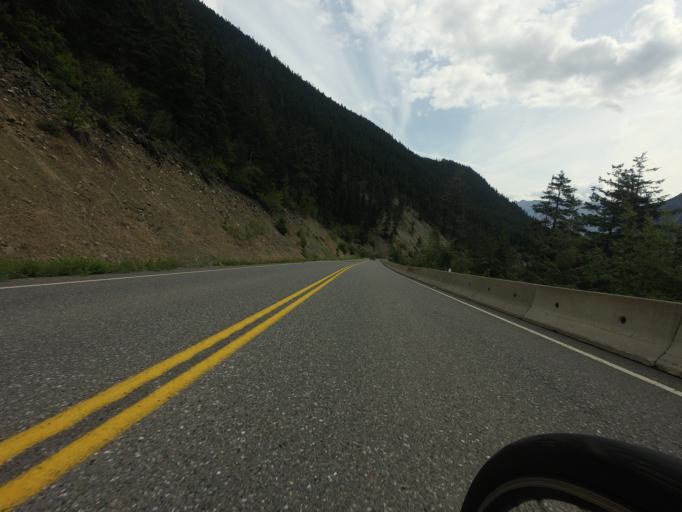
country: CA
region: British Columbia
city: Lillooet
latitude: 50.6531
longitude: -122.0137
